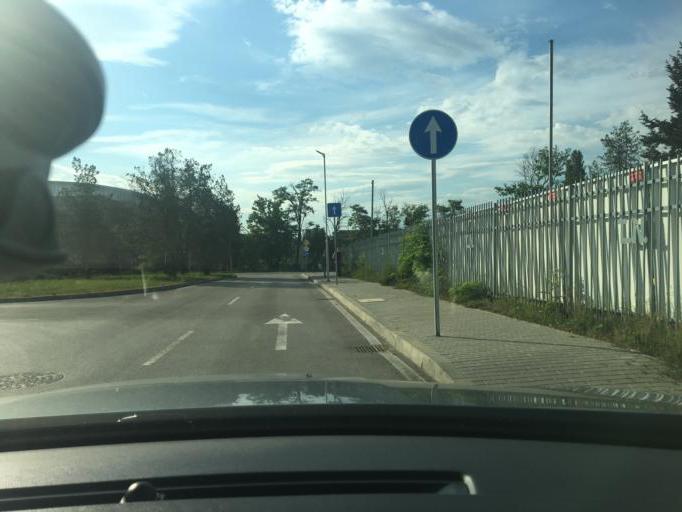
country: BG
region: Sofia-Capital
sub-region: Stolichna Obshtina
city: Sofia
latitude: 42.6704
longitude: 23.3720
